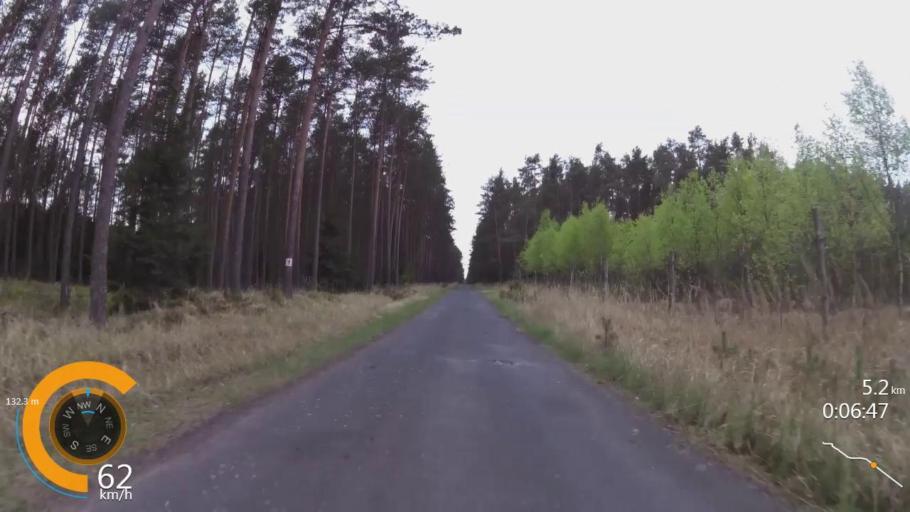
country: PL
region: West Pomeranian Voivodeship
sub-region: Powiat drawski
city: Wierzchowo
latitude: 53.4921
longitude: 16.1680
